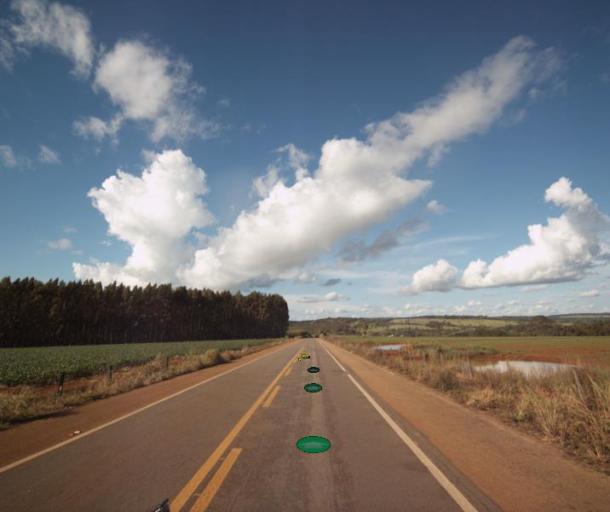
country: BR
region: Goias
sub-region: Itaberai
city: Itaberai
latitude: -16.0061
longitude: -49.7576
